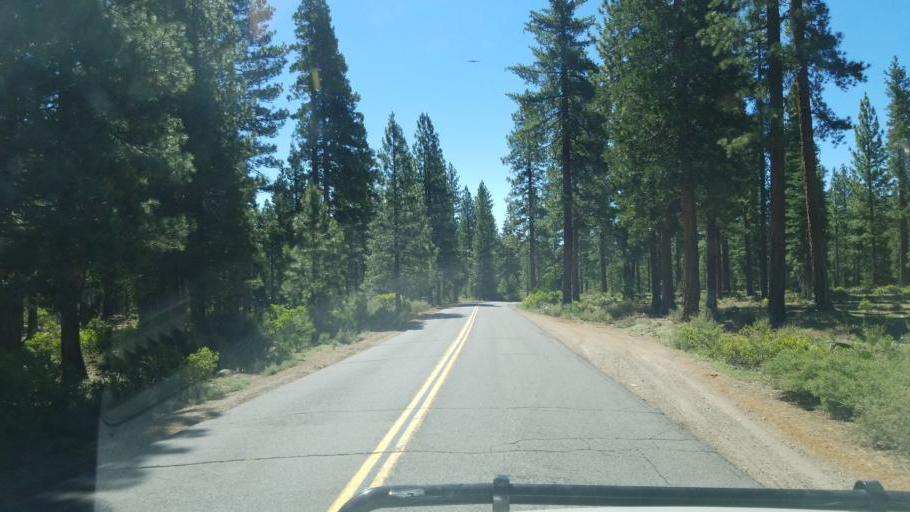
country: US
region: California
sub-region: Lassen County
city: Susanville
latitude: 40.4429
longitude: -120.7493
